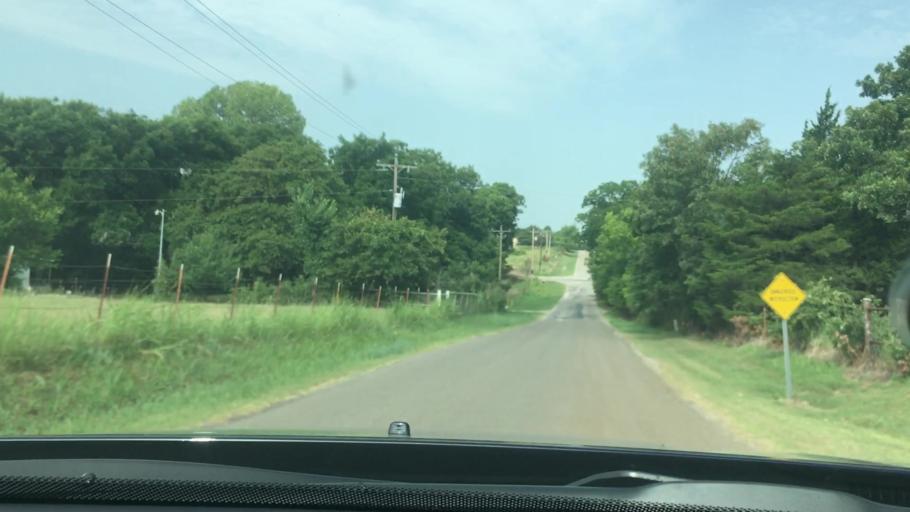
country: US
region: Oklahoma
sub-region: Garvin County
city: Pauls Valley
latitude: 34.7969
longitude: -97.1933
